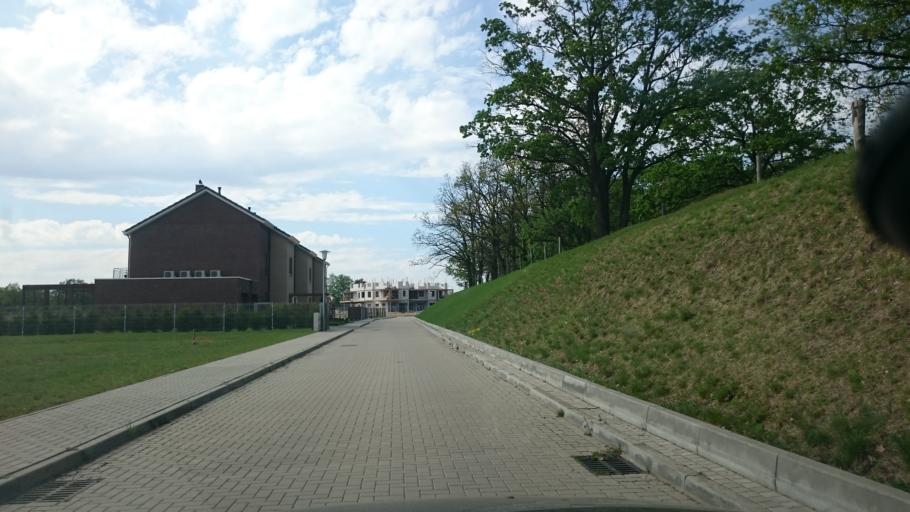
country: PL
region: Kujawsko-Pomorskie
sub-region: Grudziadz
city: Grudziadz
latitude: 53.4479
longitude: 18.7129
